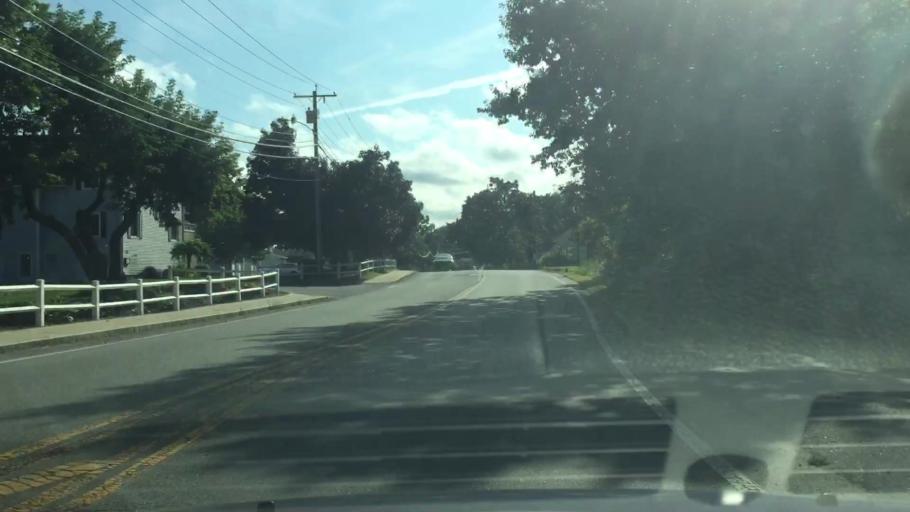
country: US
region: Massachusetts
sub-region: Middlesex County
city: Dracut
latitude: 42.6706
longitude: -71.3007
